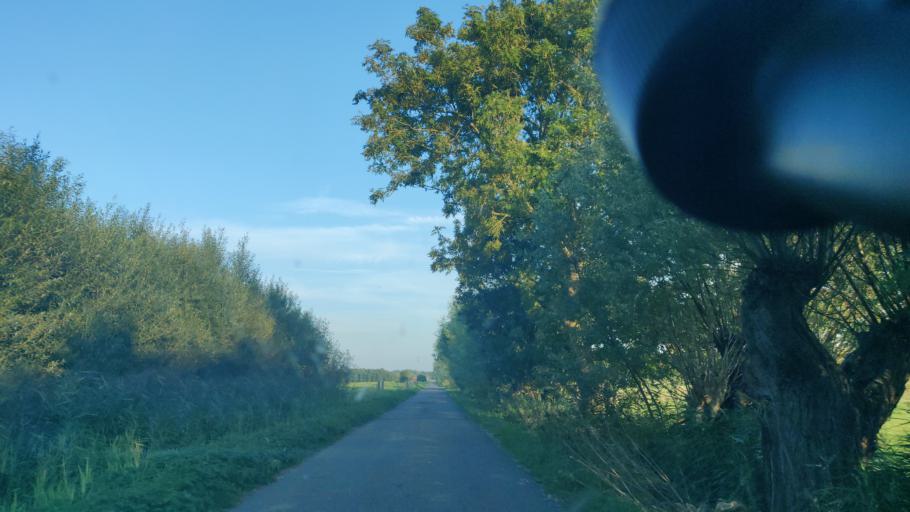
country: NL
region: South Holland
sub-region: Gemeente Voorschoten
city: Voorschoten
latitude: 52.1479
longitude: 4.4336
